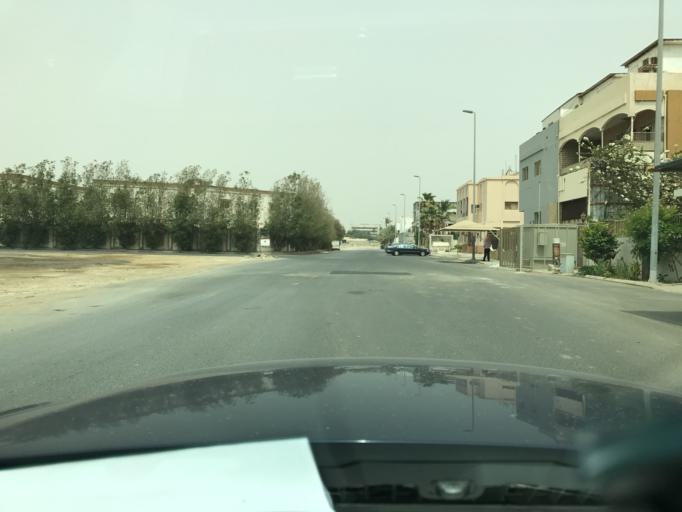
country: SA
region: Makkah
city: Jeddah
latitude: 21.5237
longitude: 39.1595
